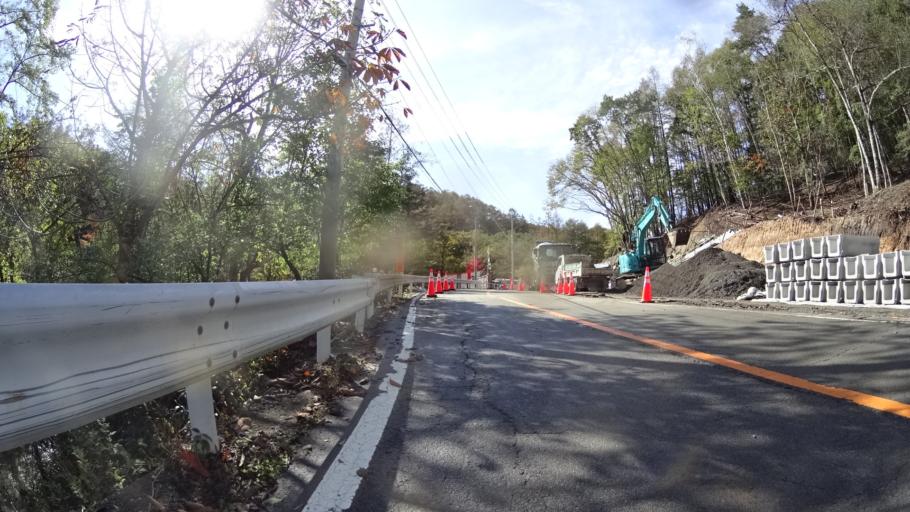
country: JP
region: Yamanashi
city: Enzan
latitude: 35.7964
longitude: 138.8098
